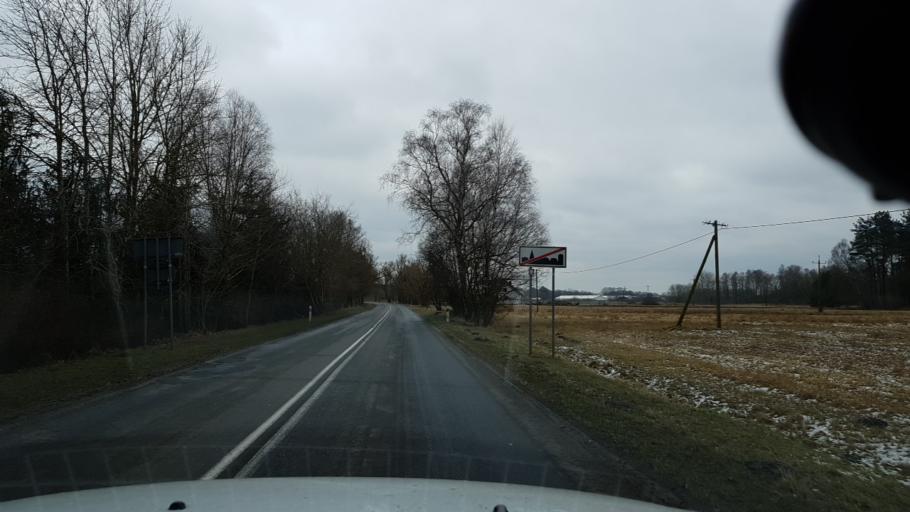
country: PL
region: West Pomeranian Voivodeship
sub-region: Powiat goleniowski
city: Goleniow
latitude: 53.6210
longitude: 14.7385
